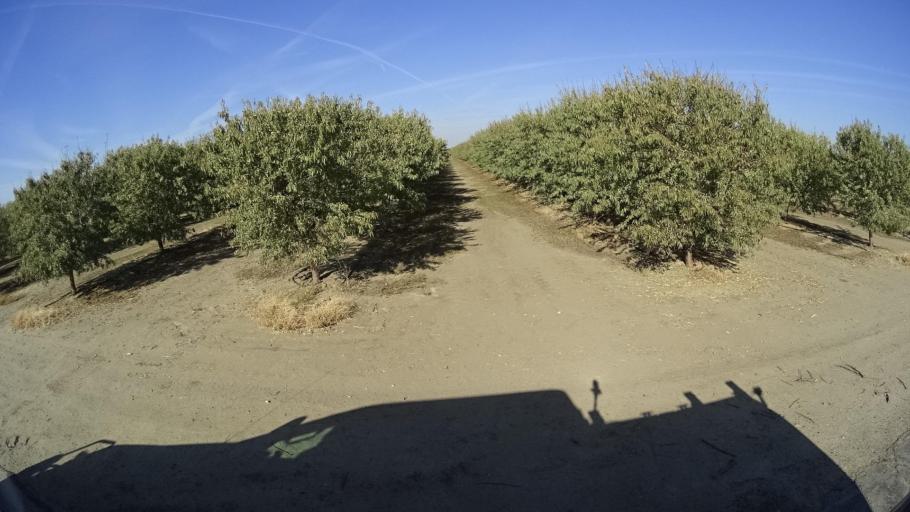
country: US
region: California
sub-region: Kern County
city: Wasco
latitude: 35.6670
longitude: -119.3815
